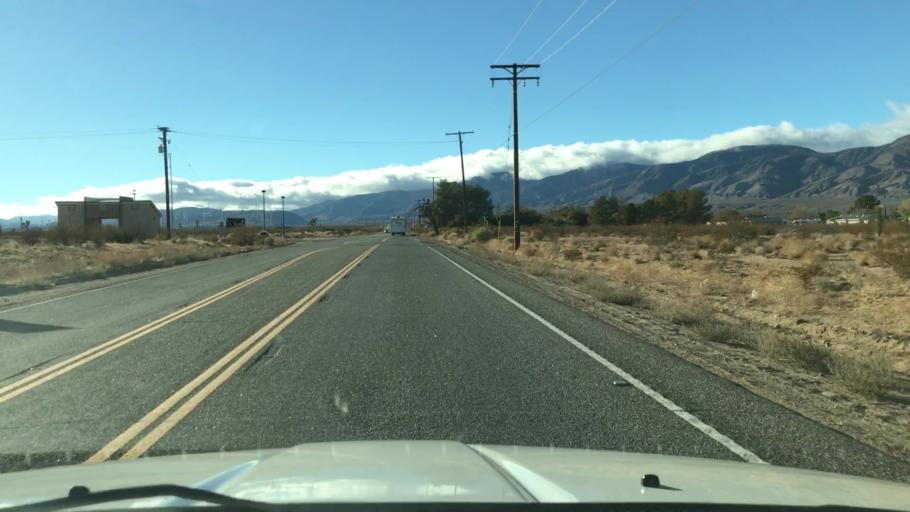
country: US
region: California
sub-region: Kern County
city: Mojave
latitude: 35.1255
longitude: -118.1097
